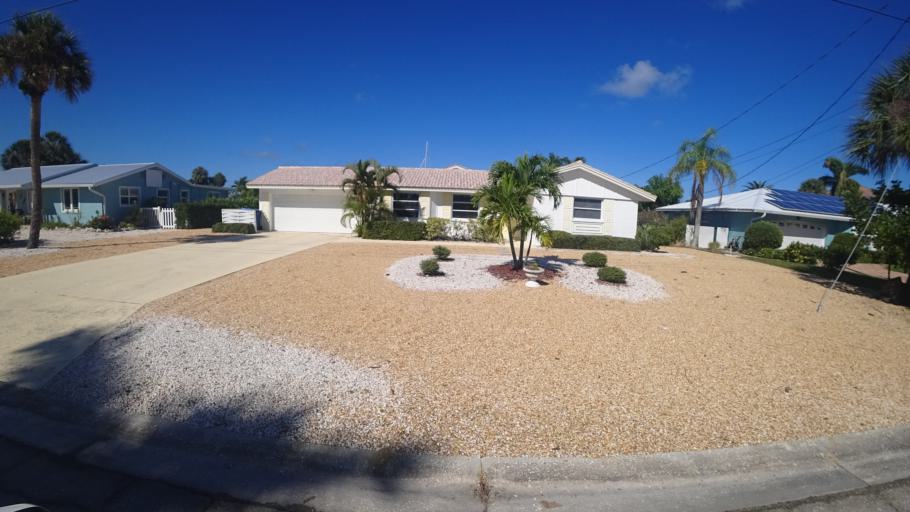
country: US
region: Florida
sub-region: Manatee County
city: Anna Maria
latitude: 27.5211
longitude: -82.7096
